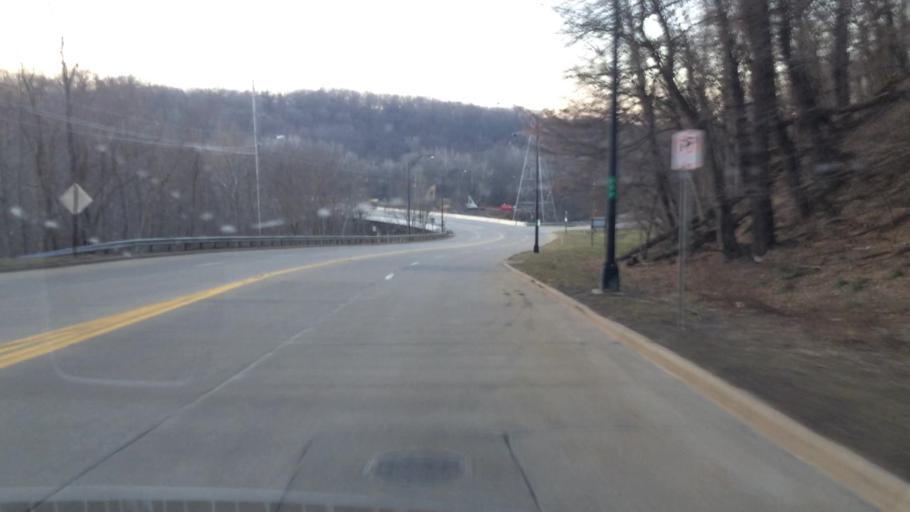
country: US
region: Ohio
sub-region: Summit County
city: Akron
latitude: 41.1021
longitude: -81.5261
